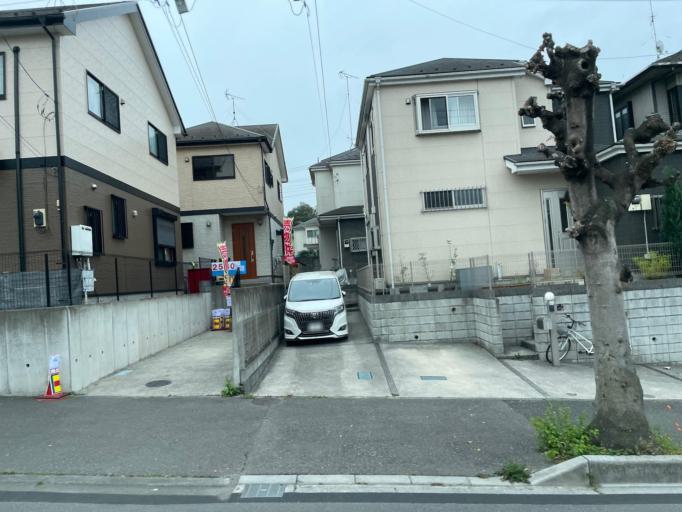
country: JP
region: Saitama
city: Saitama
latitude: 35.8882
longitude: 139.6921
